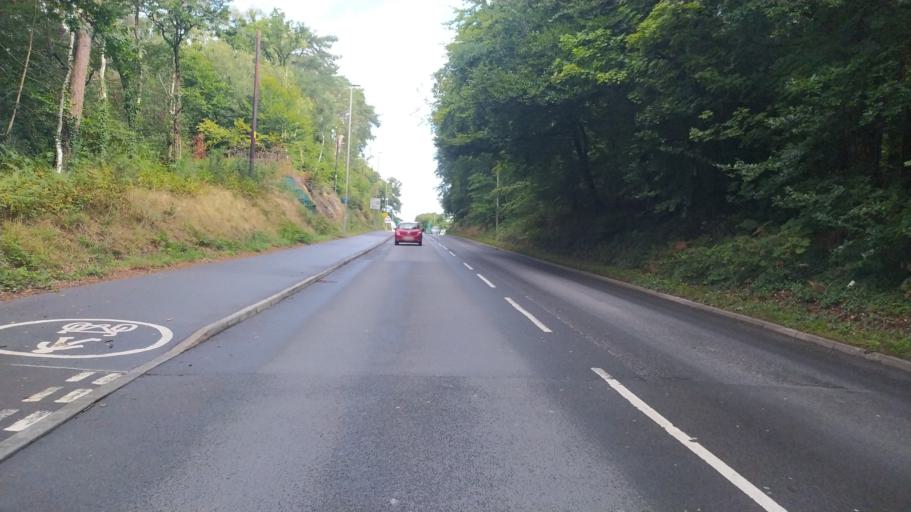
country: GB
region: England
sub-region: Dorset
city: Wimborne Minster
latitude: 50.7758
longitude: -1.9781
